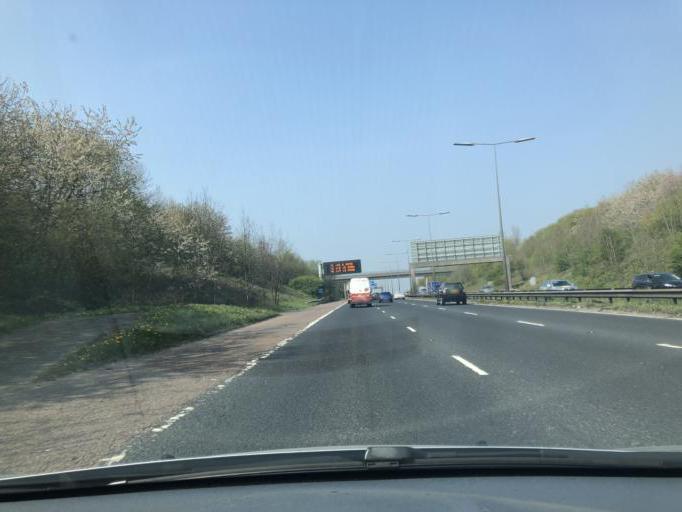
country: GB
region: England
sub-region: Borough of Tameside
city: Denton
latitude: 53.4408
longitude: -2.1316
